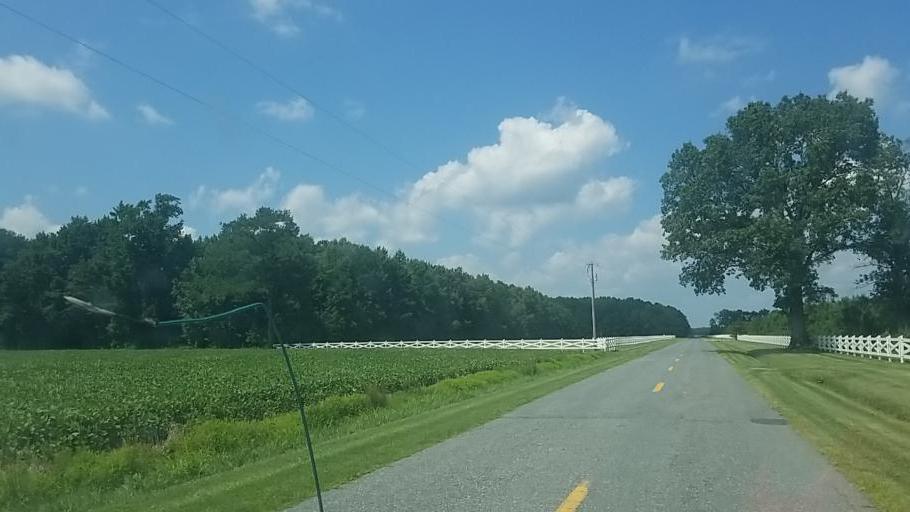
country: US
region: Maryland
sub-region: Wicomico County
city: Hebron
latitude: 38.4508
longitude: -75.8489
